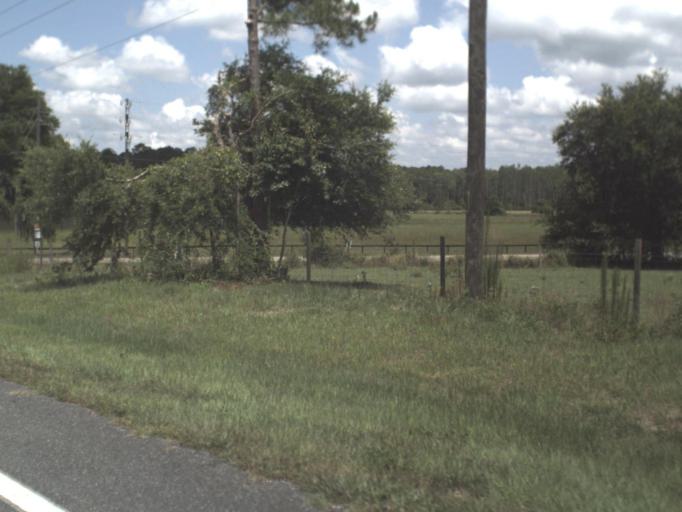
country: US
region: Florida
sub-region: Levy County
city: Williston Highlands
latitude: 29.2086
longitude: -82.5820
